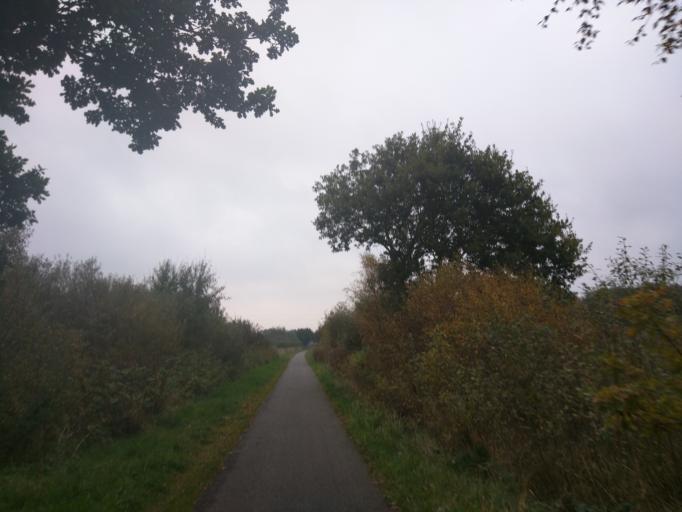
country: DK
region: Central Jutland
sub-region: Silkeborg Kommune
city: Silkeborg
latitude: 56.2248
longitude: 9.5078
